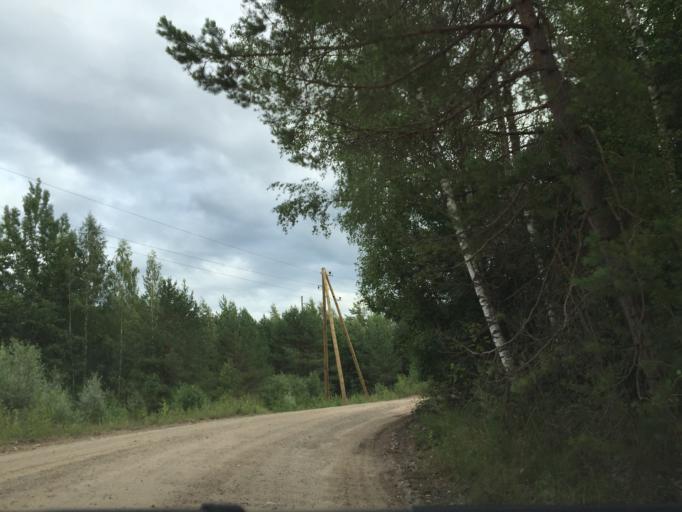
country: LV
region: Saulkrastu
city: Saulkrasti
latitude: 57.1907
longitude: 24.3635
